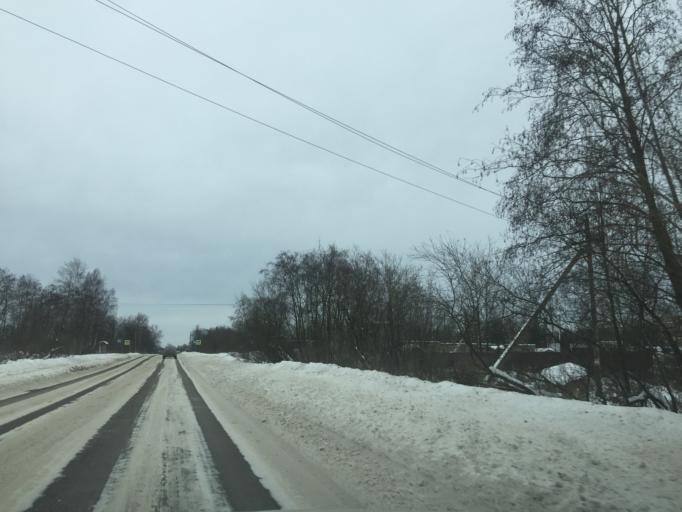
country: RU
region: Leningrad
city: Imeni Sverdlova
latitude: 59.7939
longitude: 30.6736
